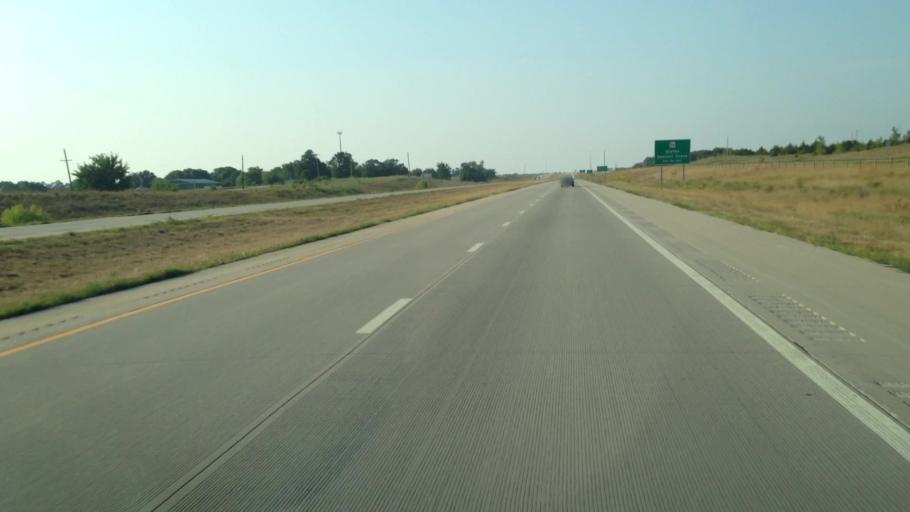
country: US
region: Kansas
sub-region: Douglas County
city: Baldwin City
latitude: 38.7675
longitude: -95.2682
